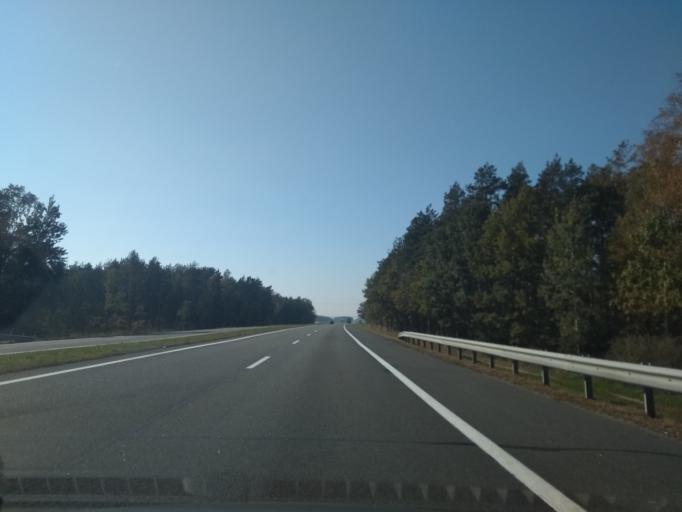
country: BY
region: Brest
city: Ivatsevichy
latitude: 52.7206
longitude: 25.4264
